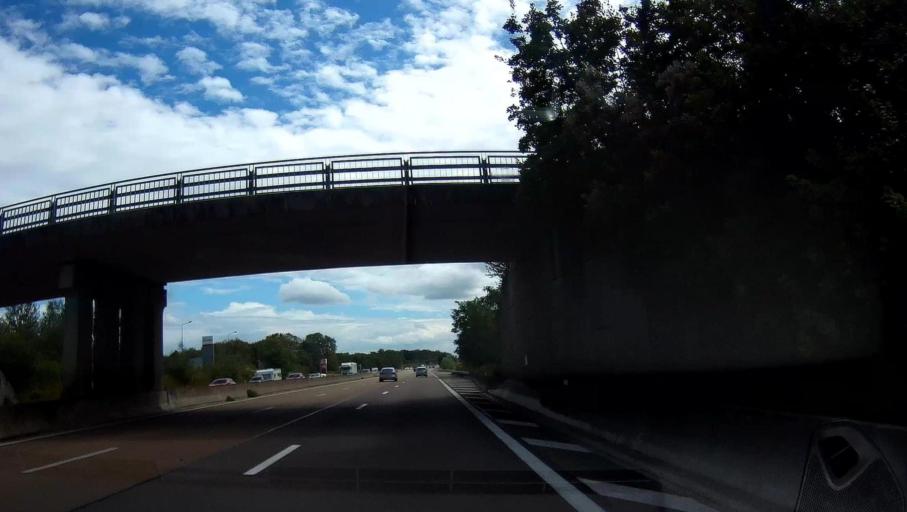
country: FR
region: Bourgogne
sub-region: Departement de la Cote-d'Or
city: Saint-Julien
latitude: 47.4248
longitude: 5.1710
